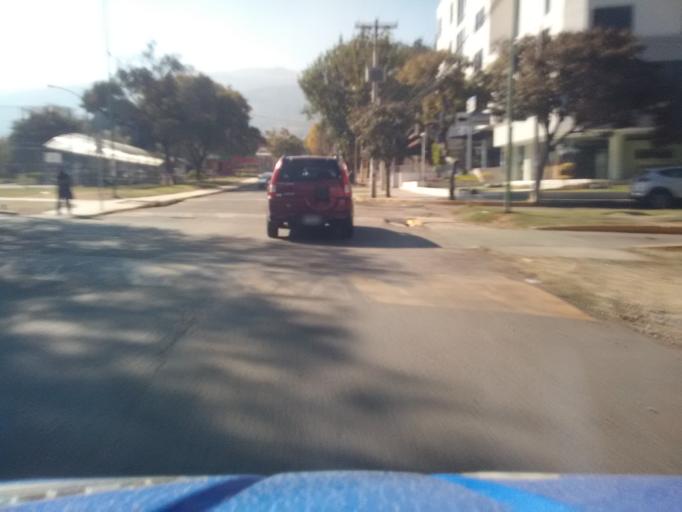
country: BO
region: Cochabamba
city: Cochabamba
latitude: -17.3717
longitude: -66.1513
